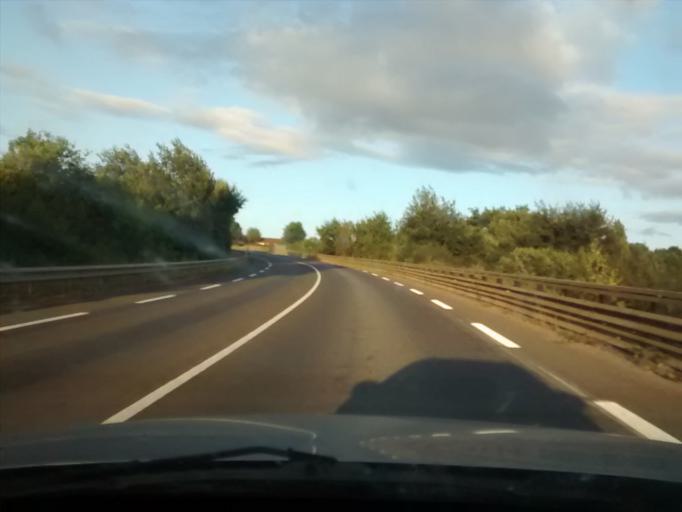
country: FR
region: Pays de la Loire
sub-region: Departement de la Sarthe
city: Saint-Saturnin
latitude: 48.0666
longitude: 0.1535
